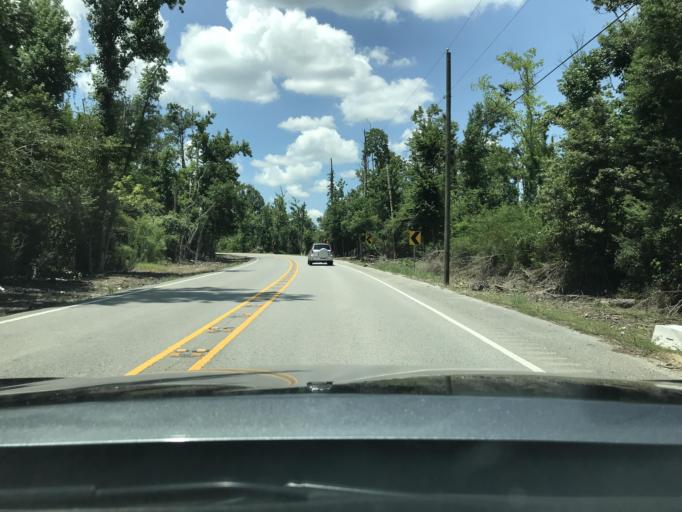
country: US
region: Louisiana
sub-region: Calcasieu Parish
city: Moss Bluff
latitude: 30.3064
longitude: -93.1808
